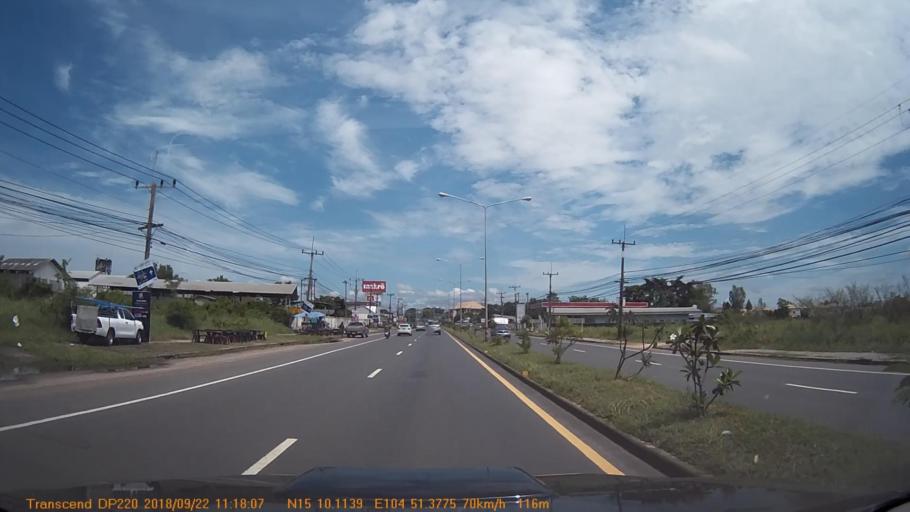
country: TH
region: Changwat Ubon Ratchathani
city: Warin Chamrap
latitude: 15.1686
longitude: 104.8563
